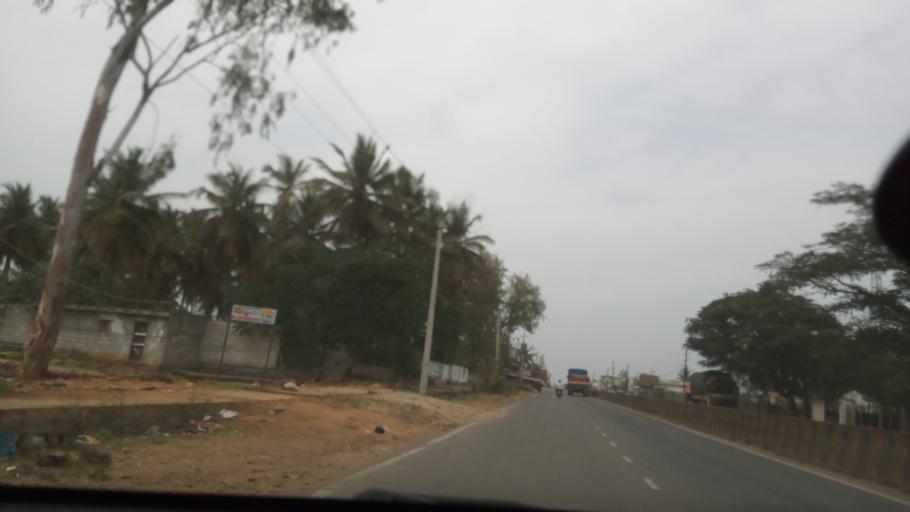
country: IN
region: Karnataka
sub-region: Chamrajnagar
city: Chamrajnagar
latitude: 11.9056
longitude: 76.9468
